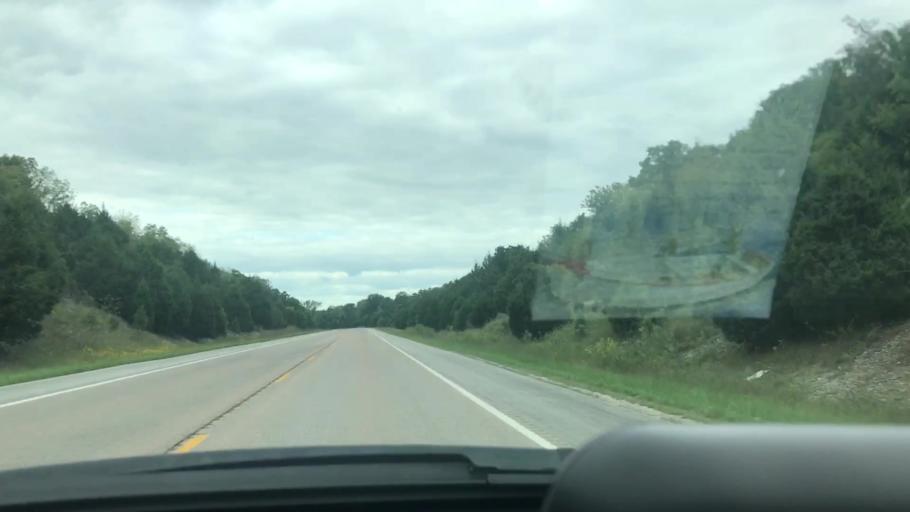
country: US
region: Missouri
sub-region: Benton County
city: Warsaw
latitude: 38.2002
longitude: -93.3257
